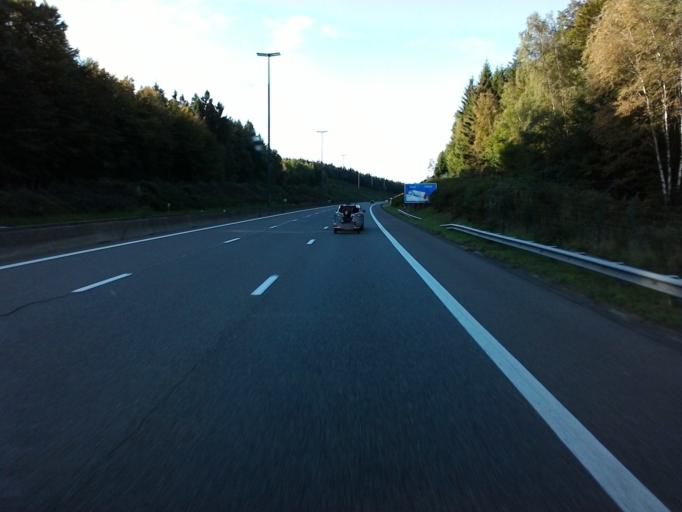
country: BE
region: Wallonia
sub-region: Province du Luxembourg
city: Houffalize
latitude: 50.1827
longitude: 5.7831
